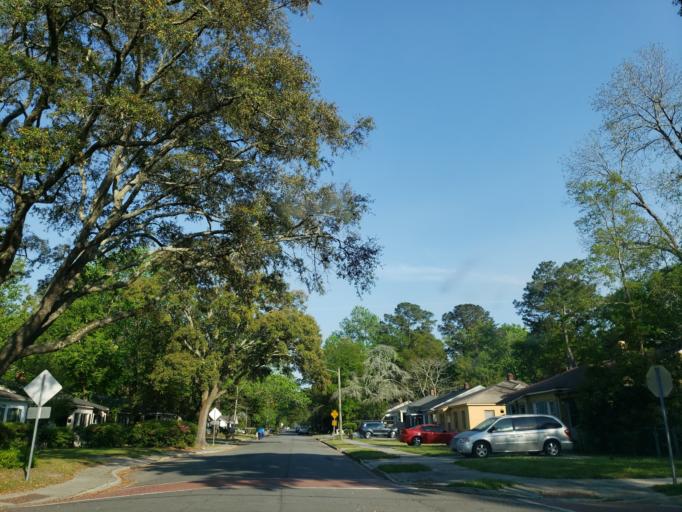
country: US
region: Georgia
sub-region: Chatham County
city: Thunderbolt
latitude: 32.0396
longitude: -81.0845
